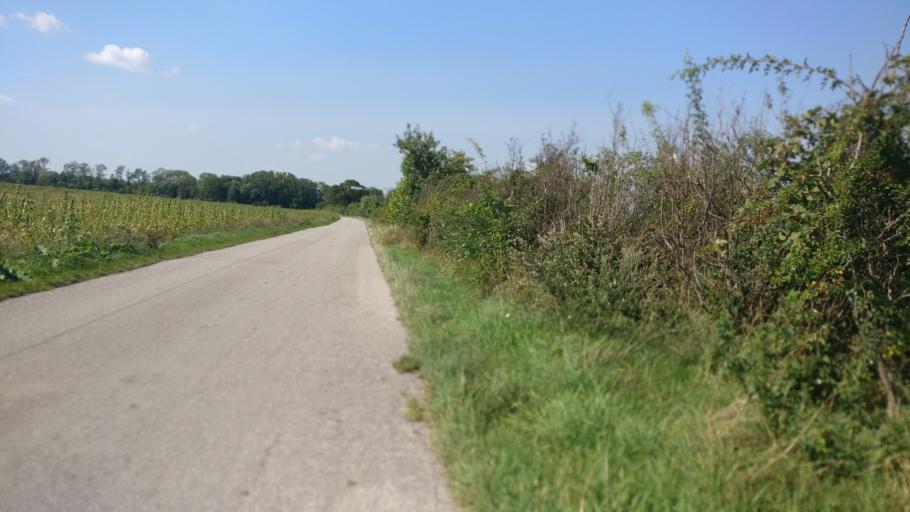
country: AT
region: Lower Austria
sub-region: Politischer Bezirk Baden
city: Mitterndorf an der Fischa
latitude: 47.9845
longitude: 16.4284
